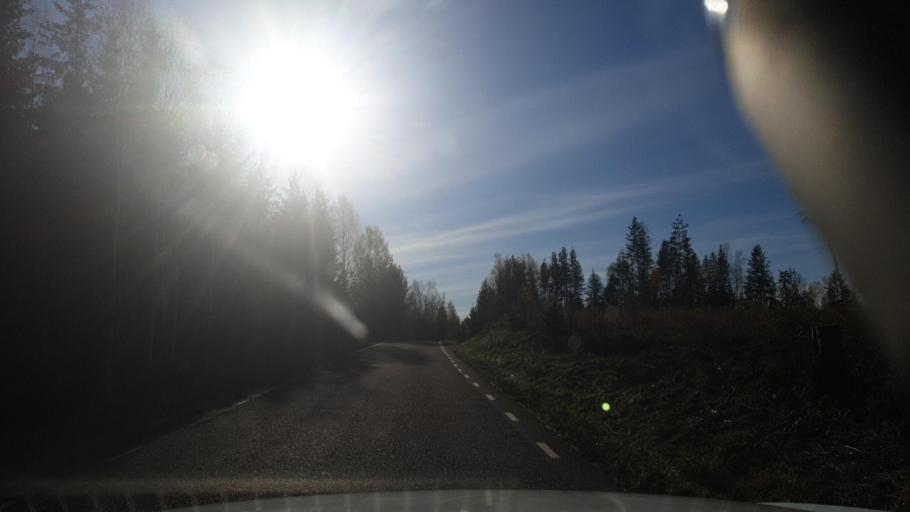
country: SE
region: Vaermland
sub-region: Karlstads Kommun
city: Edsvalla
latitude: 59.5078
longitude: 13.1104
